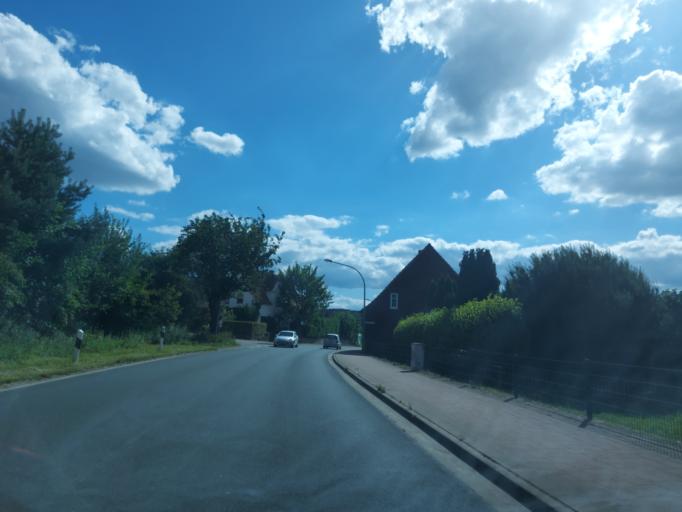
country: DE
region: Lower Saxony
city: Hagen
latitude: 52.2026
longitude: 7.9842
